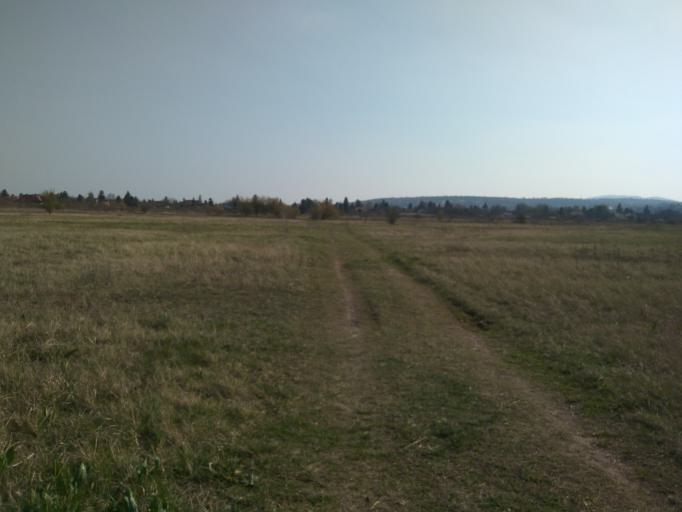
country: HU
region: Pest
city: Budakalasz
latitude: 47.6373
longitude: 19.0538
